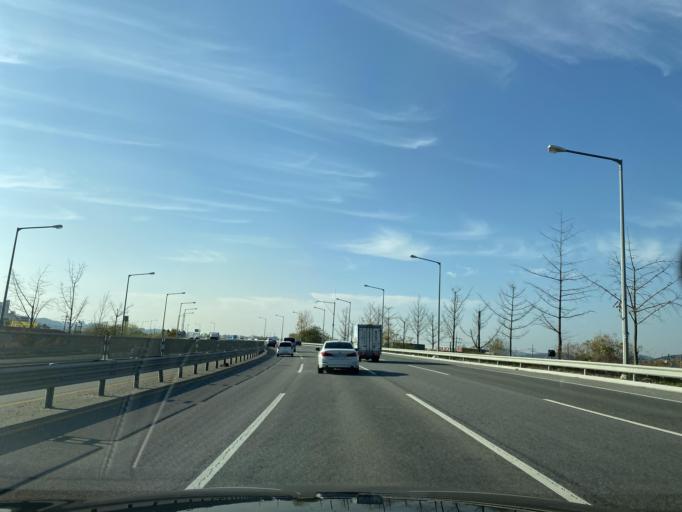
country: KR
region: Chungcheongnam-do
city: Asan
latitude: 36.7792
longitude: 127.0671
